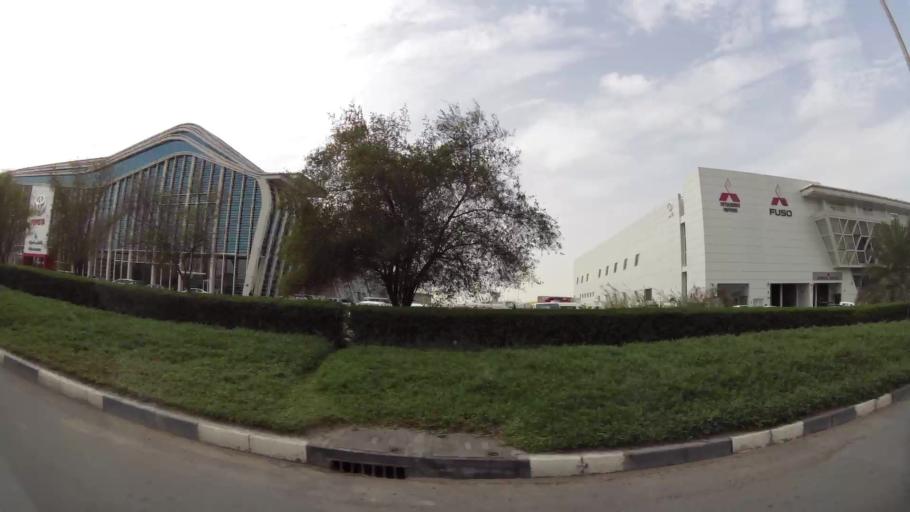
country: AE
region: Abu Dhabi
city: Abu Dhabi
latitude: 24.3425
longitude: 54.5259
